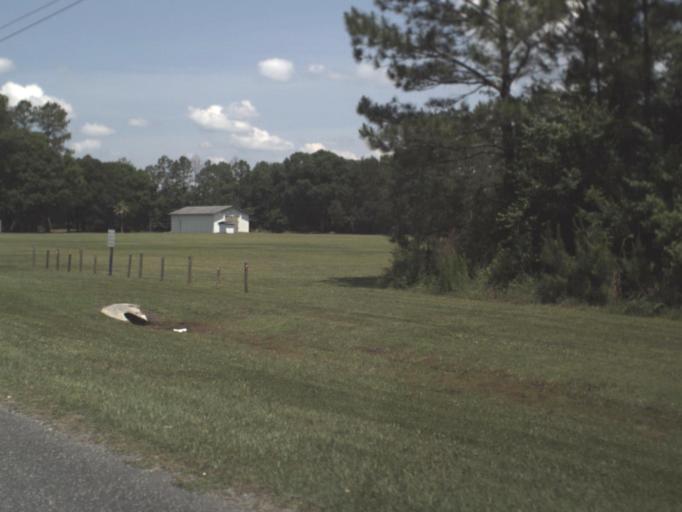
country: US
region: Florida
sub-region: Bradford County
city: Starke
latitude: 29.9605
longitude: -82.1677
